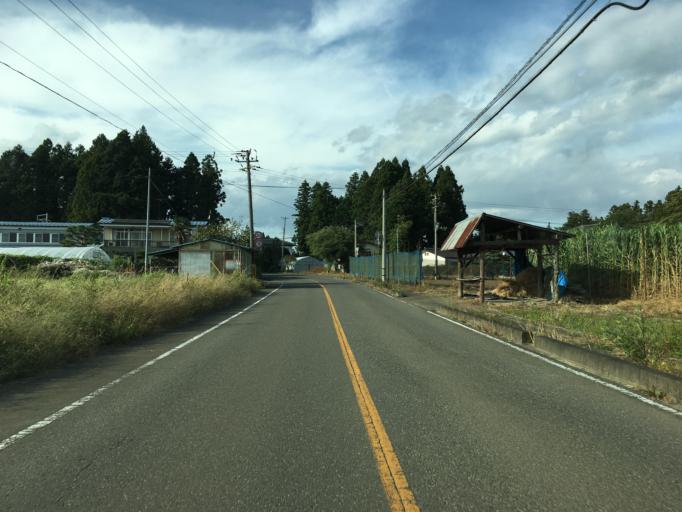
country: JP
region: Fukushima
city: Nihommatsu
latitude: 37.6190
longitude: 140.4199
